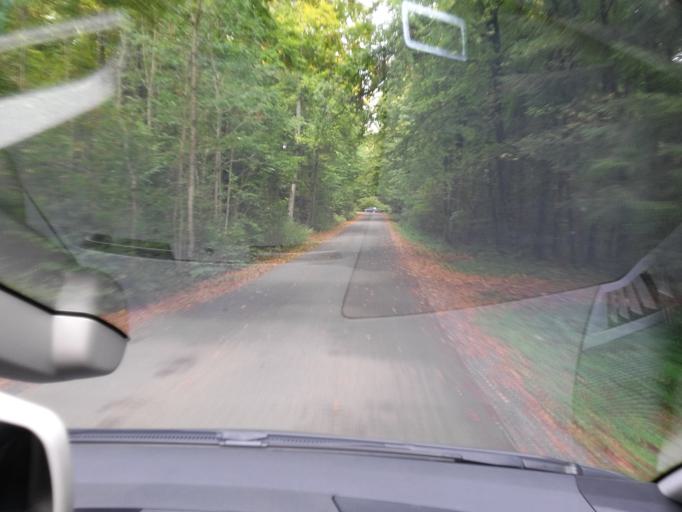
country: BE
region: Wallonia
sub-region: Province du Luxembourg
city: Attert
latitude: 49.7151
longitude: 5.7902
